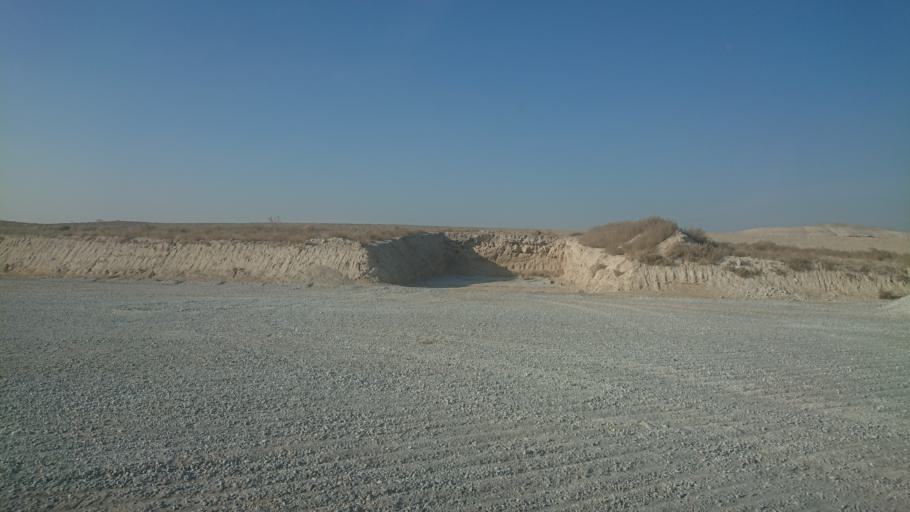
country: TR
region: Aksaray
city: Sultanhani
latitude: 38.0862
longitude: 33.6209
